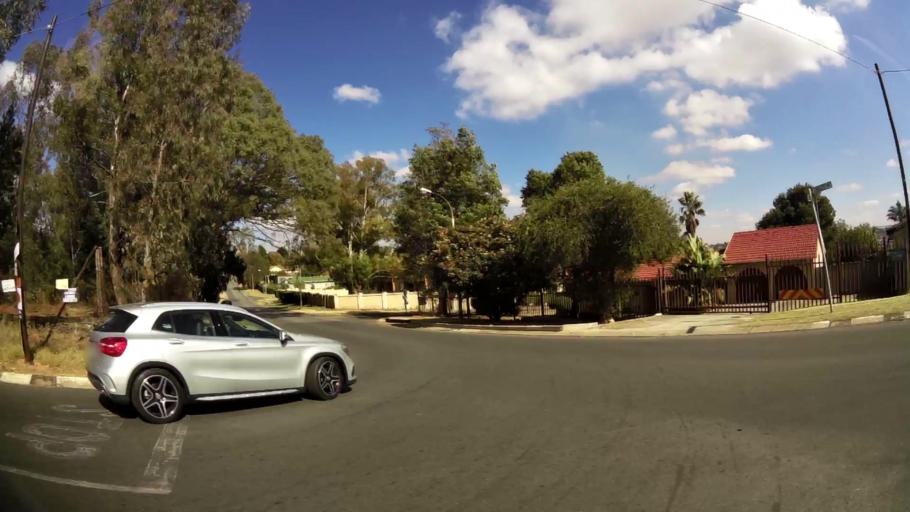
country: ZA
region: Gauteng
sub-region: City of Johannesburg Metropolitan Municipality
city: Roodepoort
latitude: -26.1240
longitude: 27.8410
